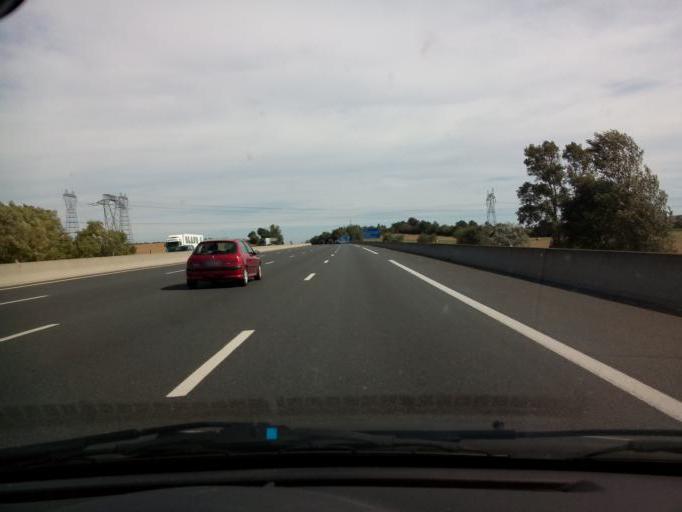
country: FR
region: Rhone-Alpes
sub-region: Departement du Rhone
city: Saint-Bonnet-de-Mure
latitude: 45.6904
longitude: 4.9898
